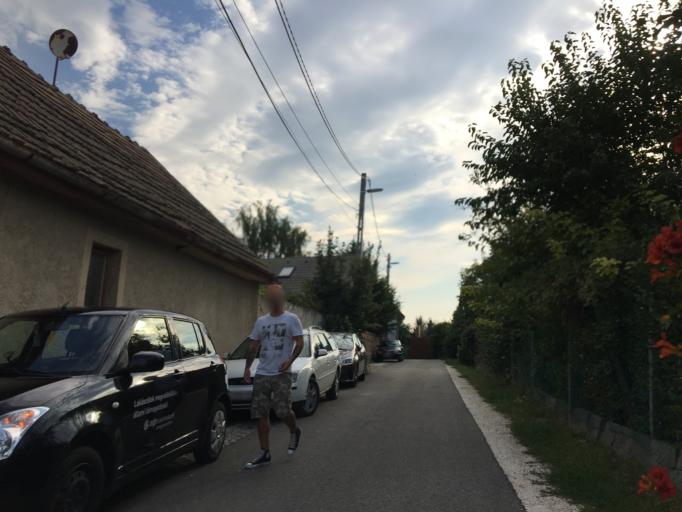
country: HU
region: Pest
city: Szigetszentmiklos
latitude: 47.3549
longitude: 19.0291
